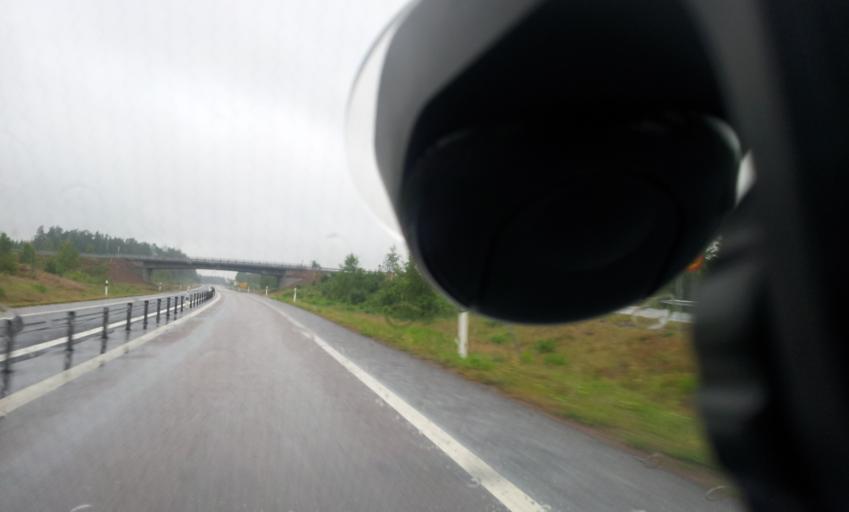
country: SE
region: Kalmar
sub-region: Oskarshamns Kommun
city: Oskarshamn
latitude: 57.3710
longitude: 16.4912
